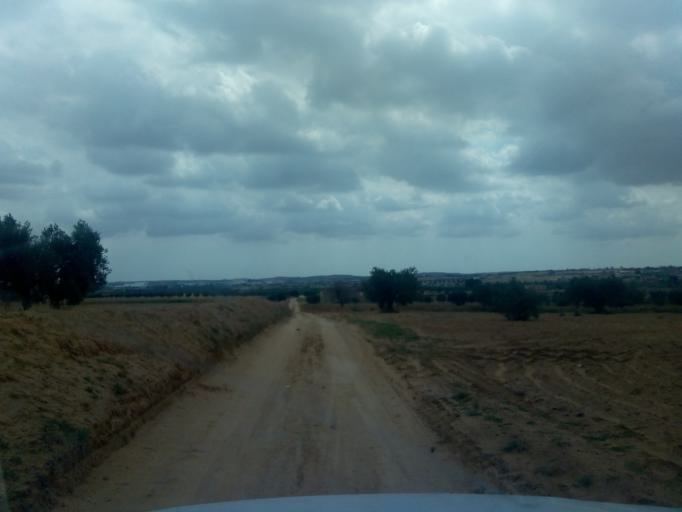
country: TN
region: Safaqis
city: Sfax
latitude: 34.7456
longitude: 10.4899
